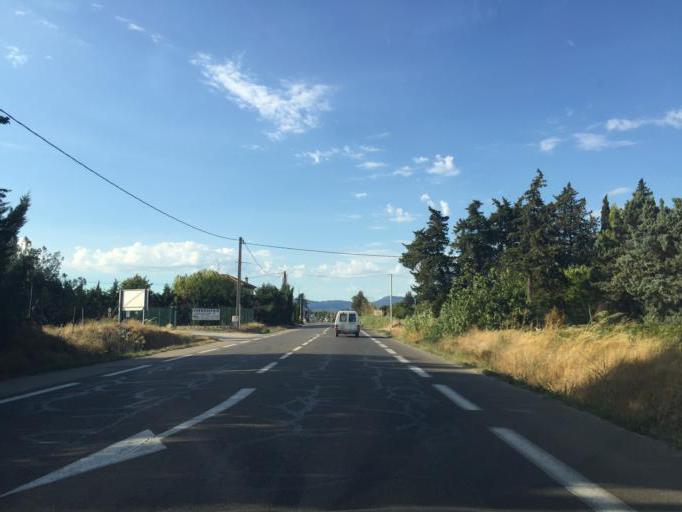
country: FR
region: Provence-Alpes-Cote d'Azur
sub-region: Departement du Vaucluse
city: Carpentras
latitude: 44.0280
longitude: 5.0523
